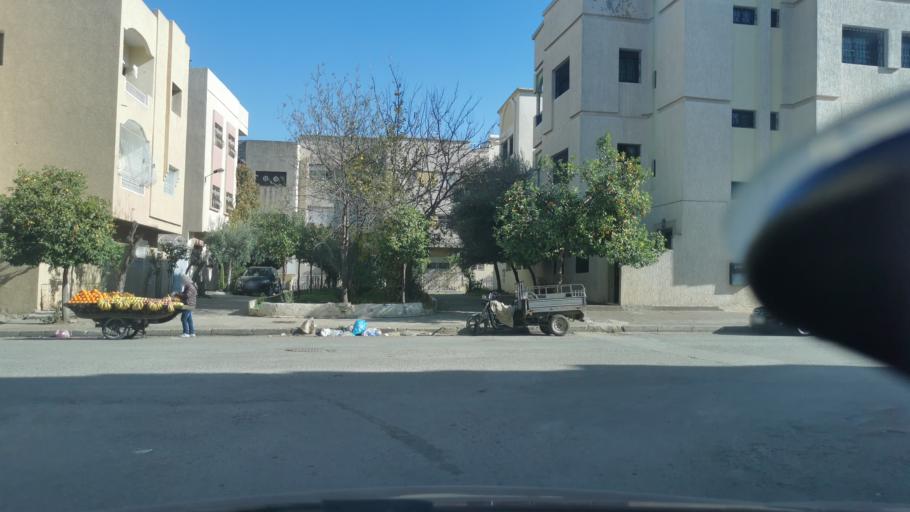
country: MA
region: Fes-Boulemane
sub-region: Fes
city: Fes
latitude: 34.0155
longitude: -4.9785
